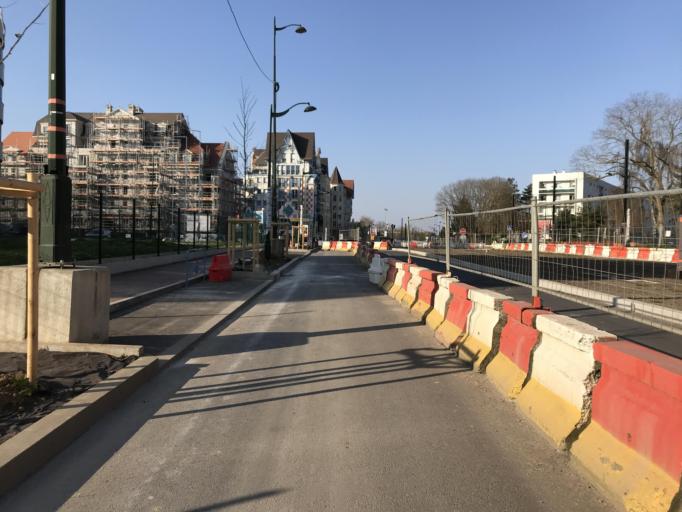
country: FR
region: Ile-de-France
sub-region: Departement des Hauts-de-Seine
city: Chatenay-Malabry
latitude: 48.7756
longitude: 2.2496
